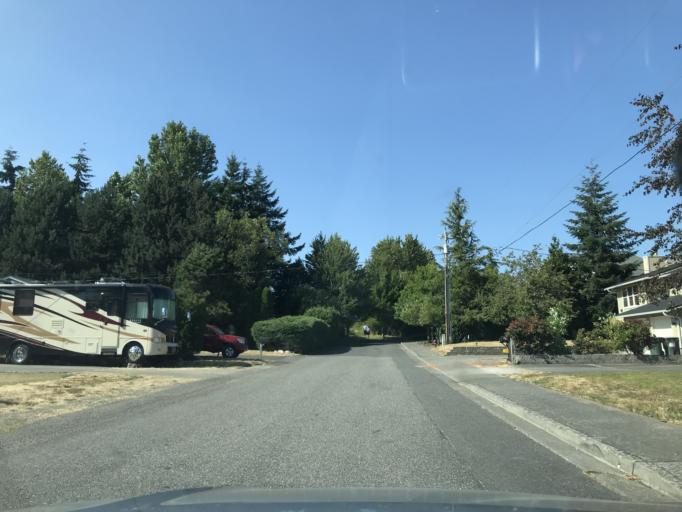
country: US
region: Washington
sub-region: Whatcom County
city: Bellingham
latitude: 48.7838
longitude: -122.5081
